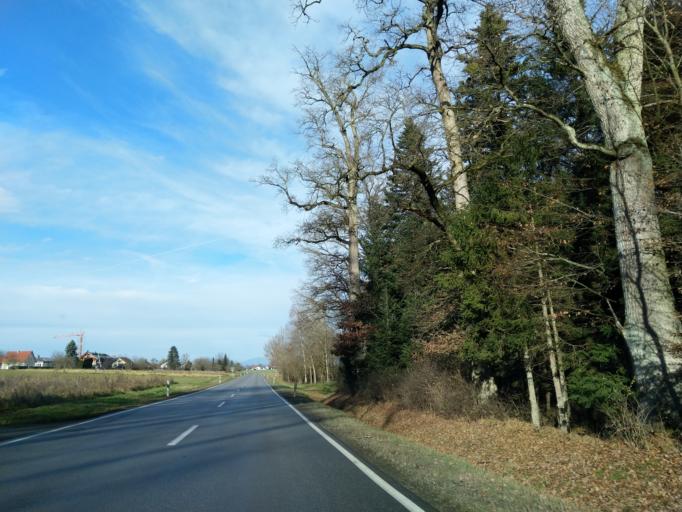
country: DE
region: Bavaria
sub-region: Lower Bavaria
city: Kunzing
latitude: 48.6367
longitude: 13.0513
